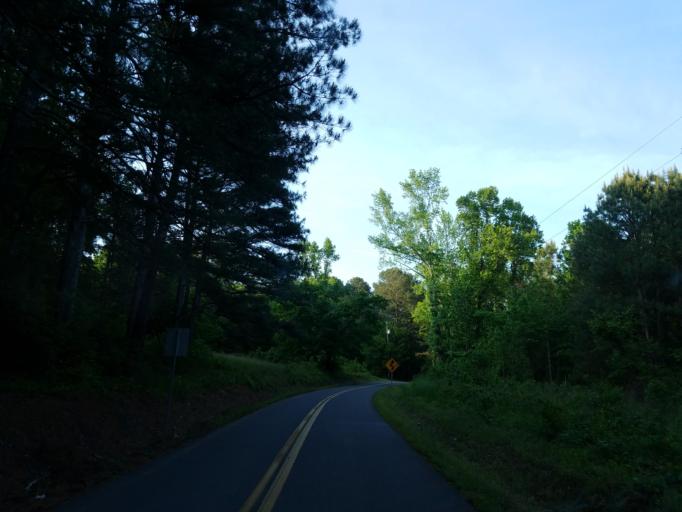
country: US
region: Georgia
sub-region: Gordon County
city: Calhoun
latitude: 34.5568
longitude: -85.1049
